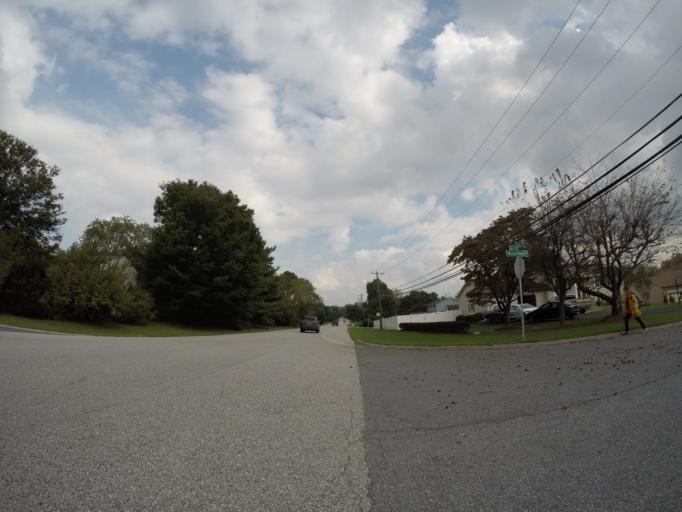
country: US
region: Maryland
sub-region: Howard County
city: Columbia
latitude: 39.2563
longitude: -76.8615
